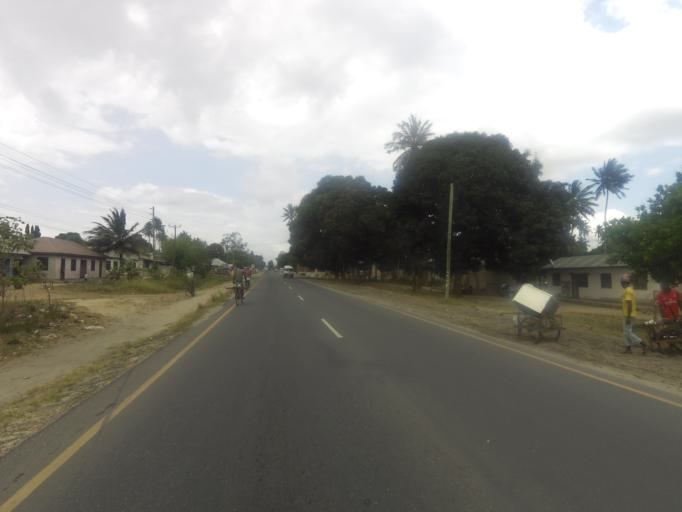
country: TZ
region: Pwani
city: Vikindu
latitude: -6.9754
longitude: 39.2873
